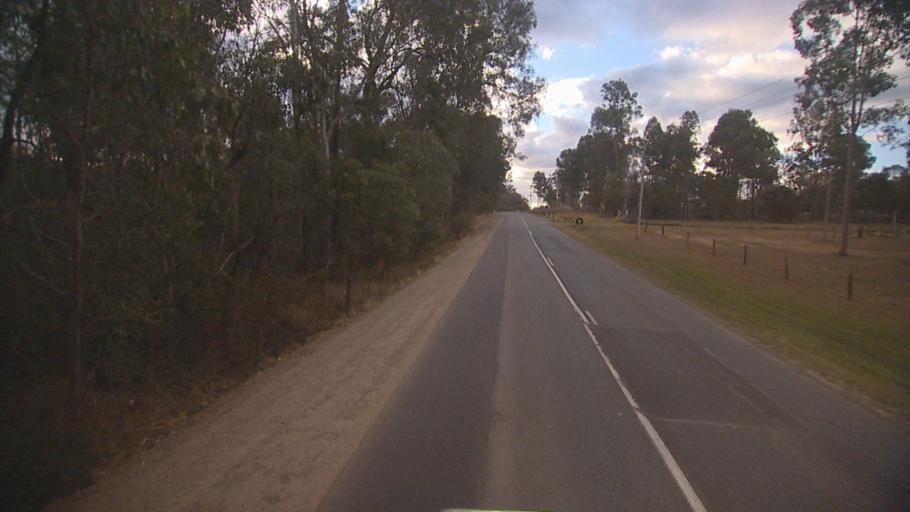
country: AU
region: Queensland
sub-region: Logan
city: Cedar Vale
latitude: -27.8586
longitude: 153.0548
